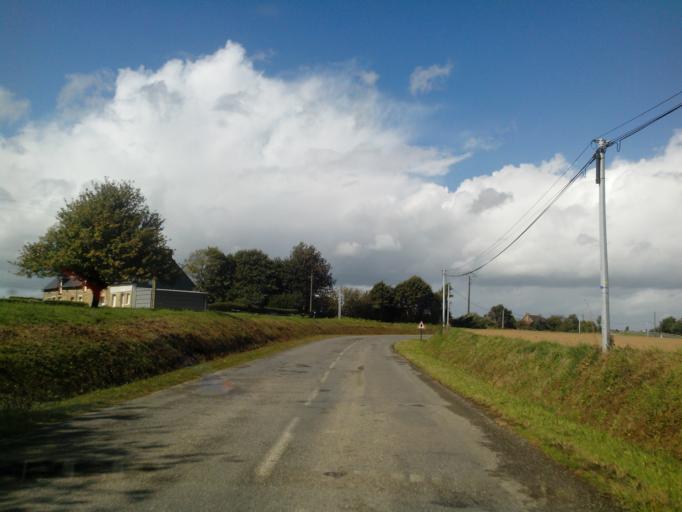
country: FR
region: Brittany
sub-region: Departement des Cotes-d'Armor
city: Merdrignac
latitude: 48.1817
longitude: -2.4135
